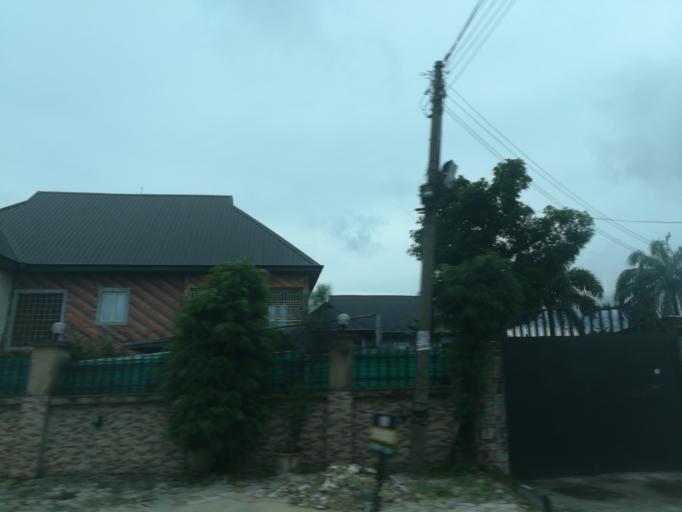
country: NG
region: Rivers
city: Port Harcourt
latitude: 4.8204
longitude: 6.9989
